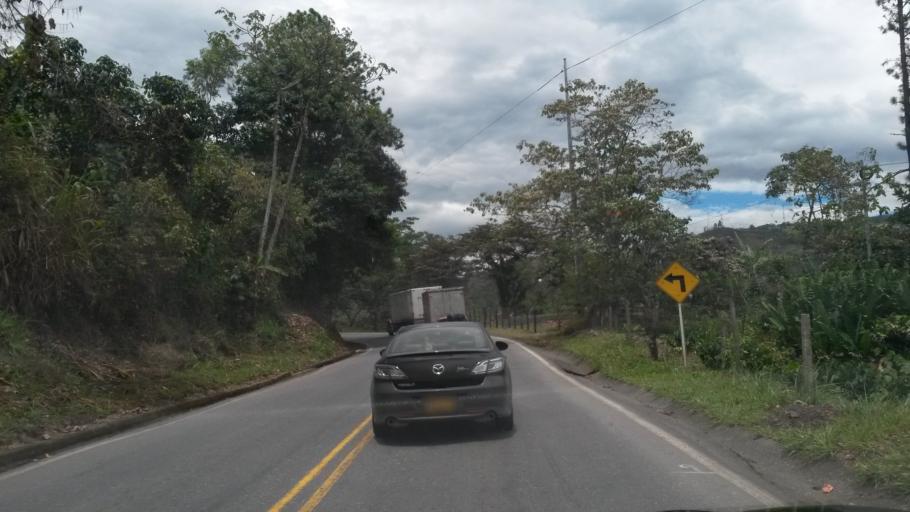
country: CO
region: Cauca
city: Rosas
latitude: 2.2573
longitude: -76.7566
